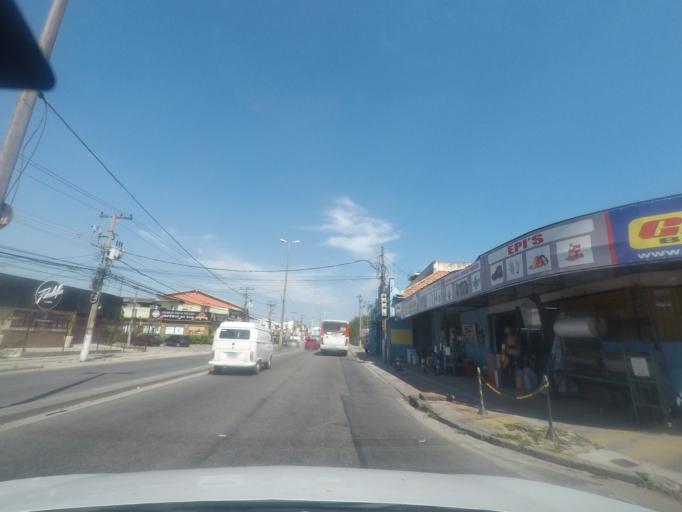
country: BR
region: Rio de Janeiro
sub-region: Nilopolis
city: Nilopolis
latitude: -22.8775
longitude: -43.4438
